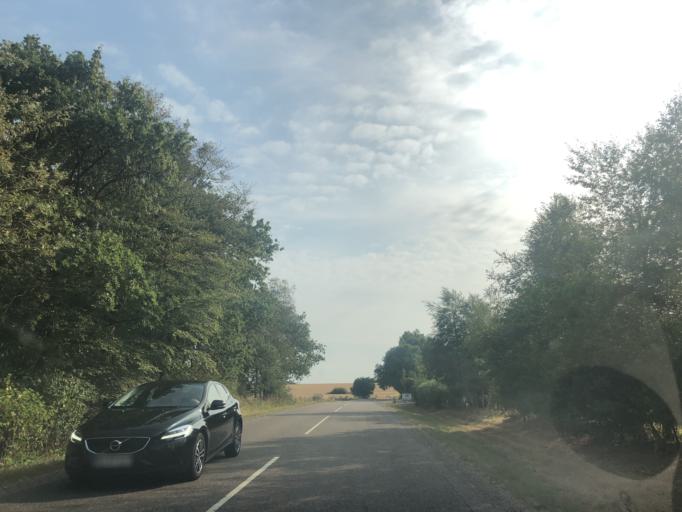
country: DK
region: Central Jutland
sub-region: Skive Kommune
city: Skive
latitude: 56.6824
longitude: 8.9708
